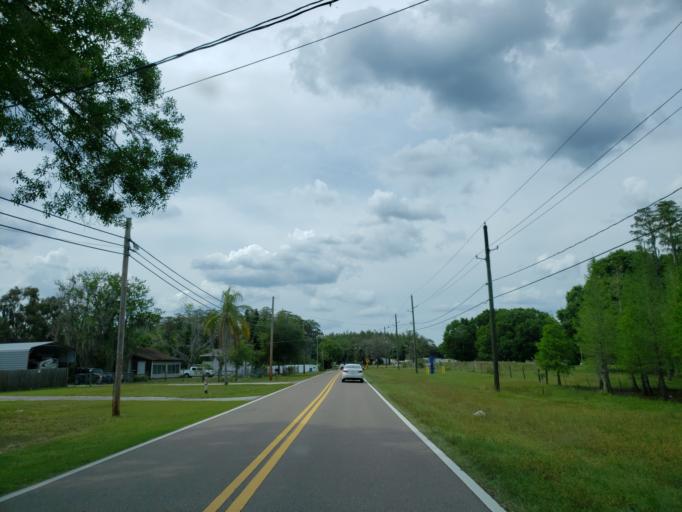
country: US
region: Florida
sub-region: Hillsborough County
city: Keystone
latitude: 28.1273
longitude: -82.6150
